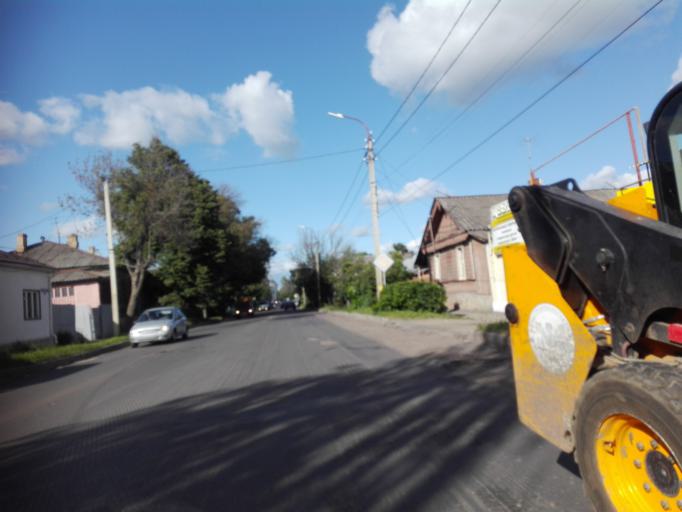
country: RU
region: Orjol
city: Orel
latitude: 52.9576
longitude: 36.0551
